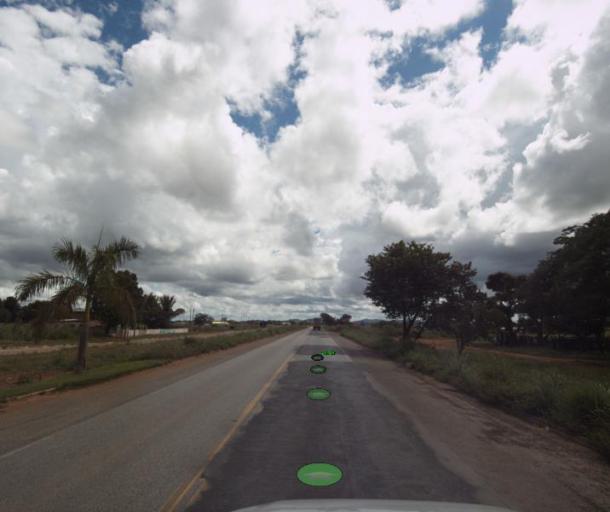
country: BR
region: Goias
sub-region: Uruacu
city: Uruacu
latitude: -14.3024
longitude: -49.1480
